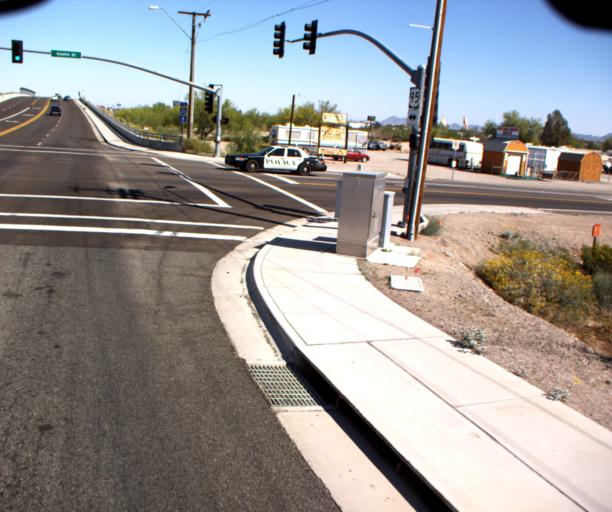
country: US
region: Arizona
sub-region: La Paz County
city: Quartzsite
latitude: 33.6600
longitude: -114.2170
